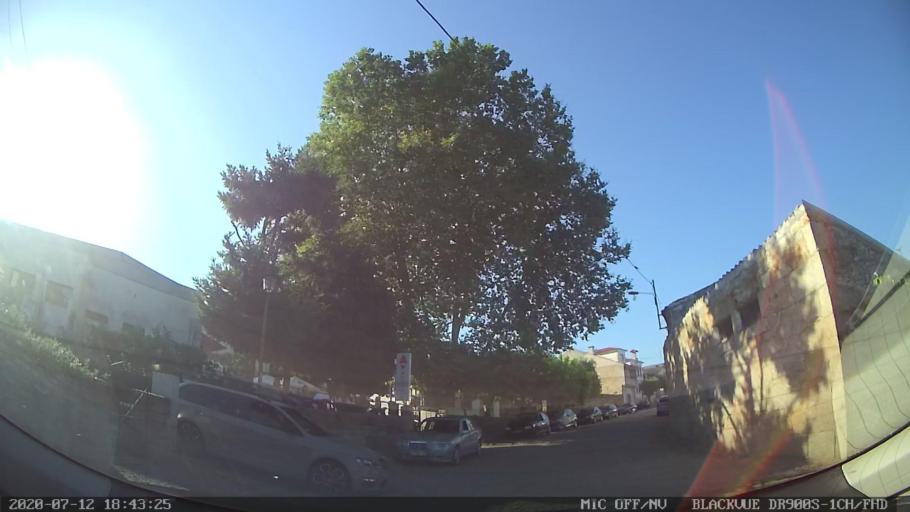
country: PT
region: Viseu
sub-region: Sao Joao da Pesqueira
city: Sao Joao da Pesqueira
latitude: 41.2488
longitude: -7.4332
